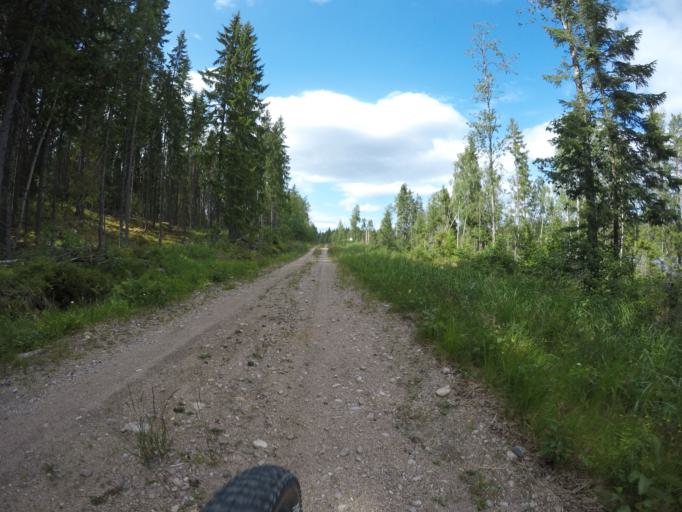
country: SE
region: Dalarna
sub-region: Ludvika Kommun
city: Abborrberget
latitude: 60.0336
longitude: 14.5988
